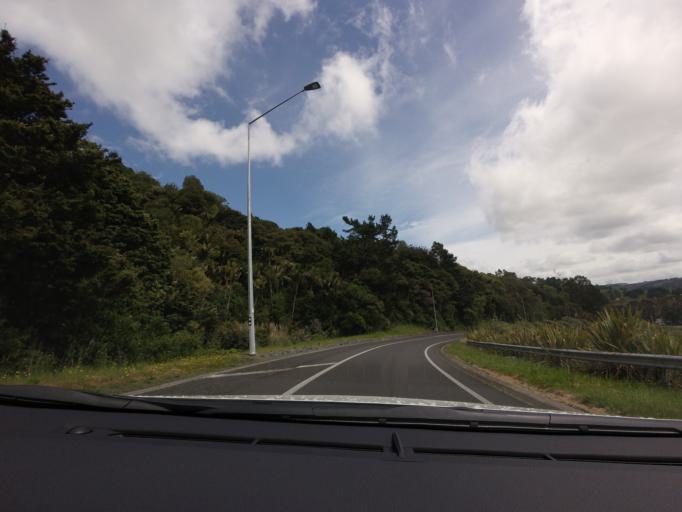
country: NZ
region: Auckland
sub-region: Auckland
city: Warkworth
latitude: -36.5340
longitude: 174.6792
